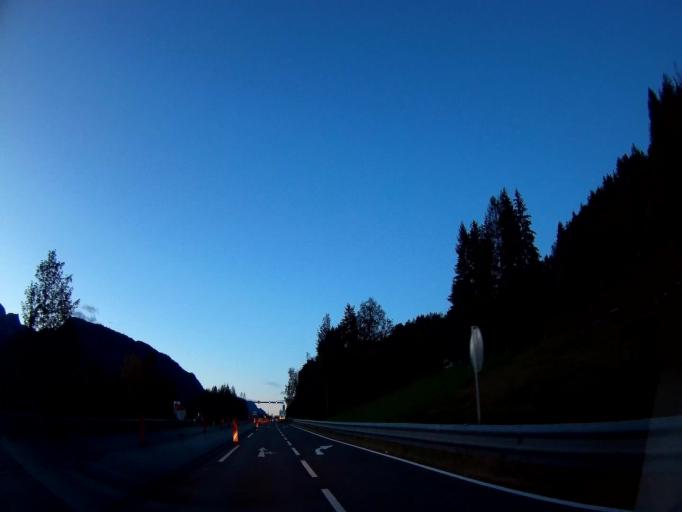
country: AT
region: Salzburg
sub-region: Politischer Bezirk Sankt Johann im Pongau
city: Bischofshofen
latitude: 47.4030
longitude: 13.2262
